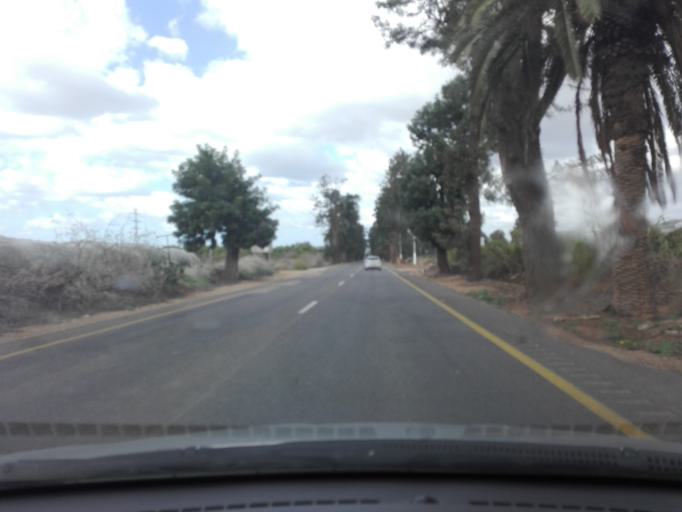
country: IL
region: Haifa
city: Qesarya
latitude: 32.4957
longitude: 34.9654
